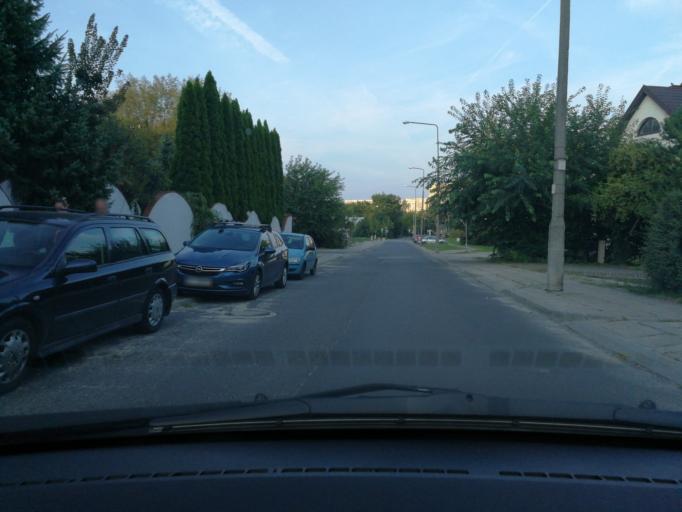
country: PL
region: Masovian Voivodeship
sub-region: Warszawa
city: Zoliborz
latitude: 52.2808
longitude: 20.9646
